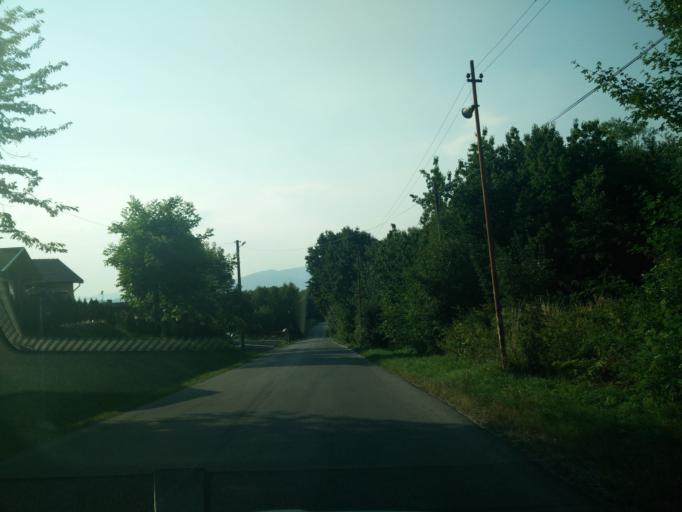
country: SK
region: Nitriansky
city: Prievidza
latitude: 48.7550
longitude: 18.6630
